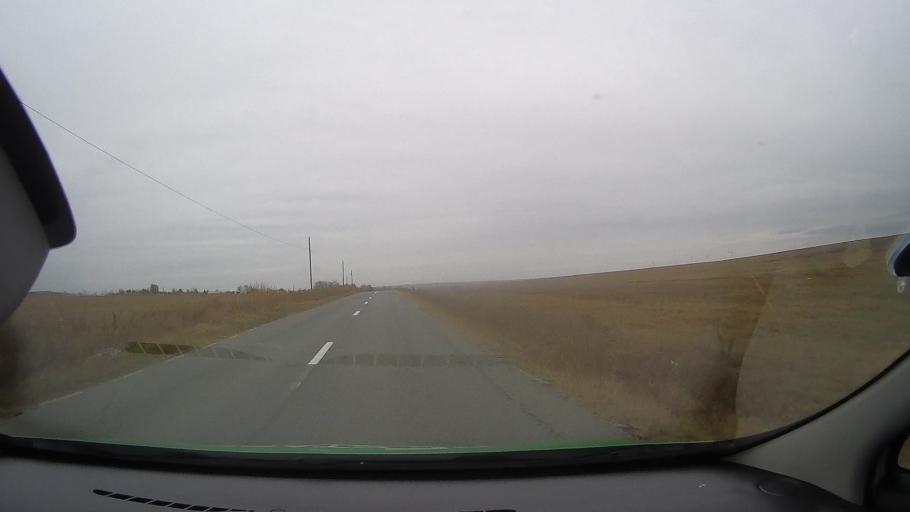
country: RO
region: Constanta
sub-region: Comuna Silistea
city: Silistea
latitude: 44.4381
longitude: 28.2270
